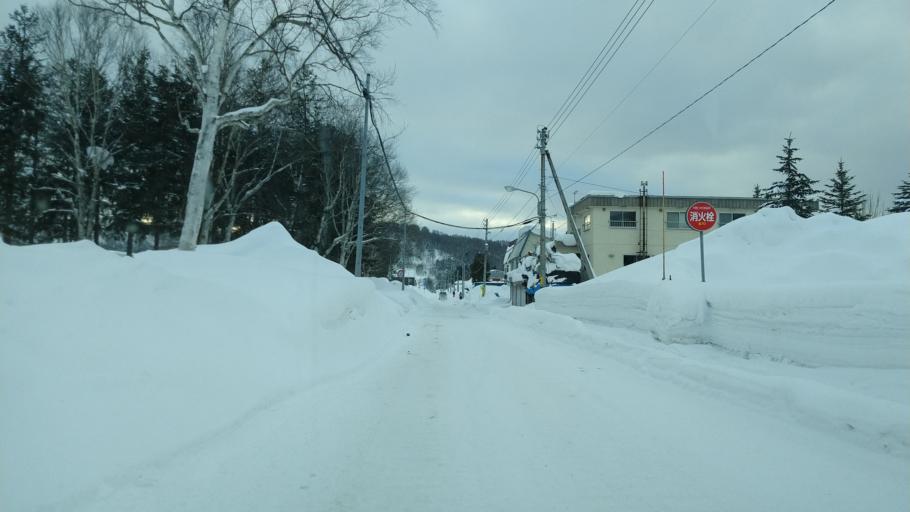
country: JP
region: Hokkaido
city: Niseko Town
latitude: 42.9090
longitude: 140.7522
